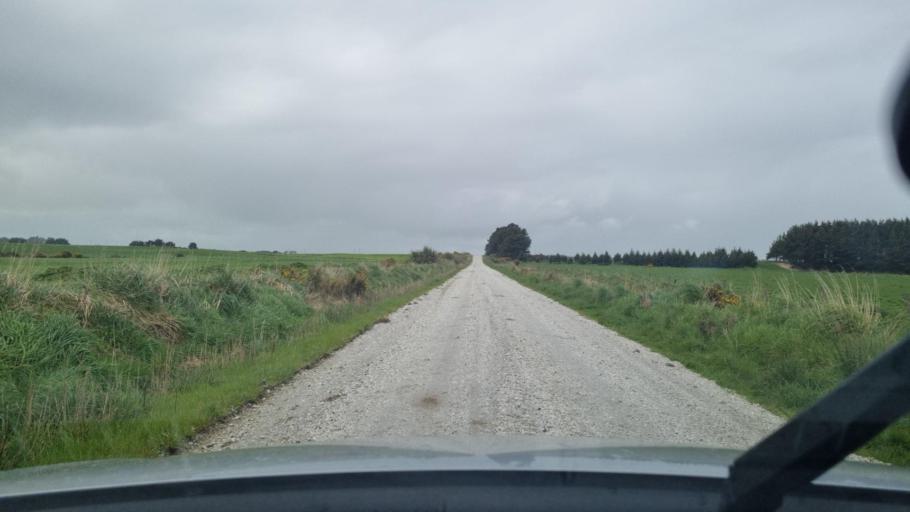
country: NZ
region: Southland
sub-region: Invercargill City
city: Invercargill
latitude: -46.5028
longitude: 168.4042
